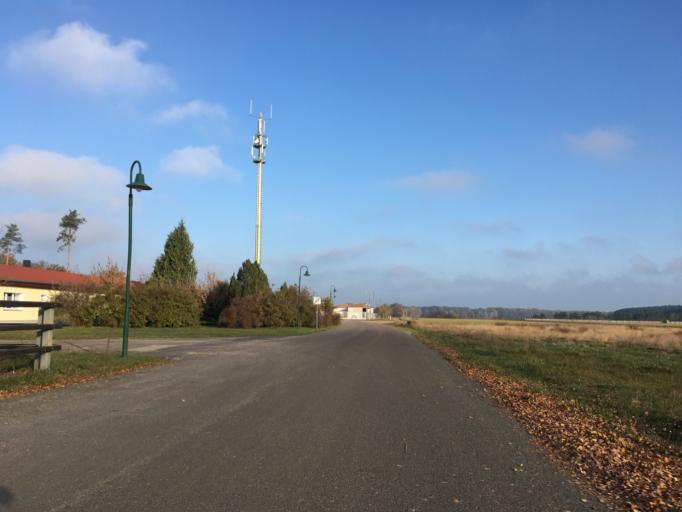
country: DE
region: Brandenburg
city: Schlepzig
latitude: 52.0331
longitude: 13.9042
